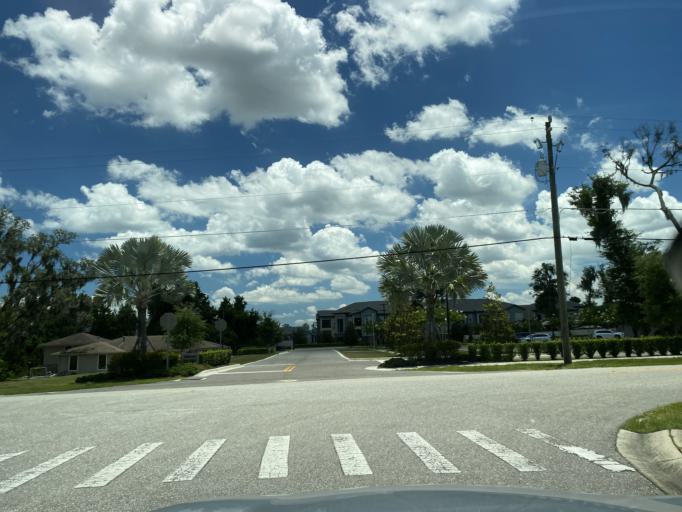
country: US
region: Florida
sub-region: Seminole County
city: Heathrow
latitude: 28.8128
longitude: -81.3581
